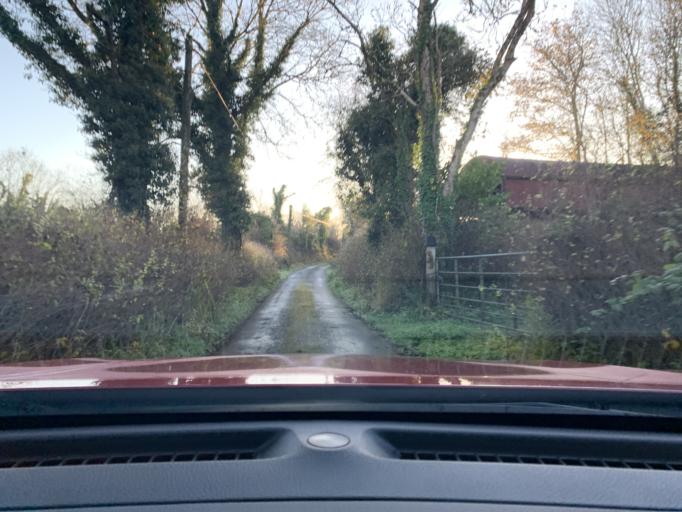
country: IE
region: Connaught
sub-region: Sligo
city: Ballymote
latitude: 53.9843
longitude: -8.5141
